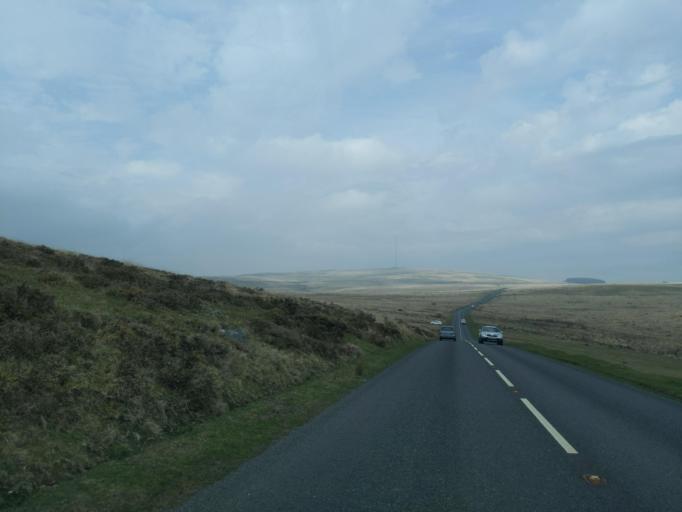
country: GB
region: England
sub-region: Devon
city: Yelverton
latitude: 50.5230
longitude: -4.0238
